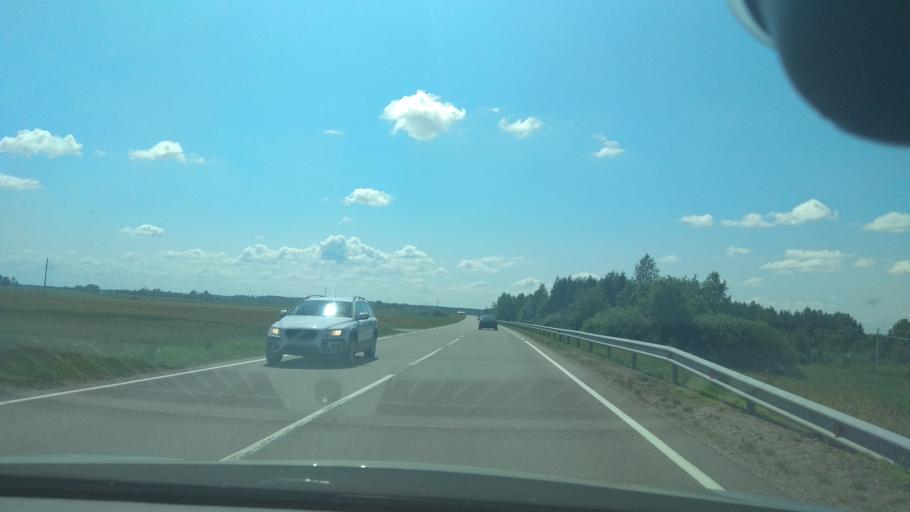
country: LT
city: Seda
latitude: 56.1690
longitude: 22.1123
